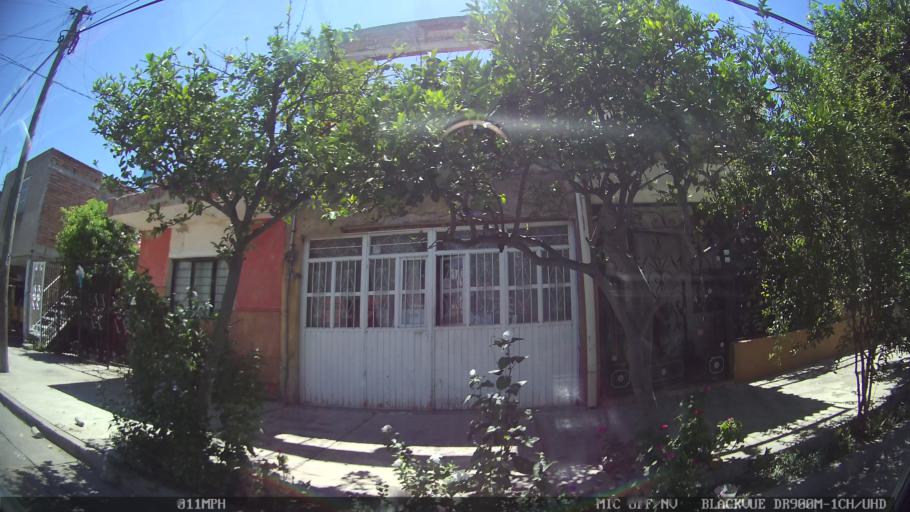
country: MX
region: Jalisco
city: Tlaquepaque
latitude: 20.6635
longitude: -103.2739
